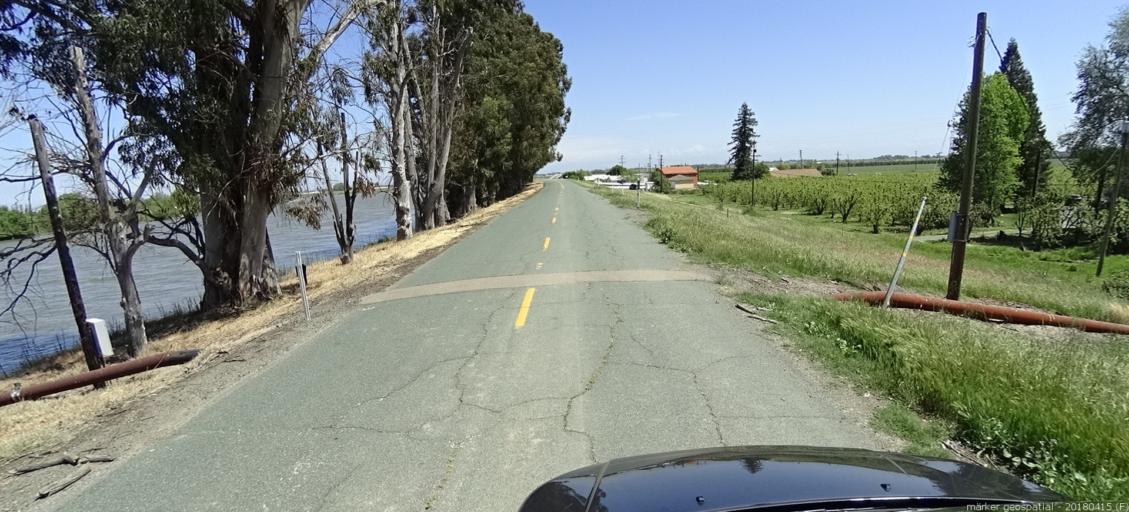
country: US
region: California
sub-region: Solano County
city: Rio Vista
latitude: 38.1936
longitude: -121.6187
